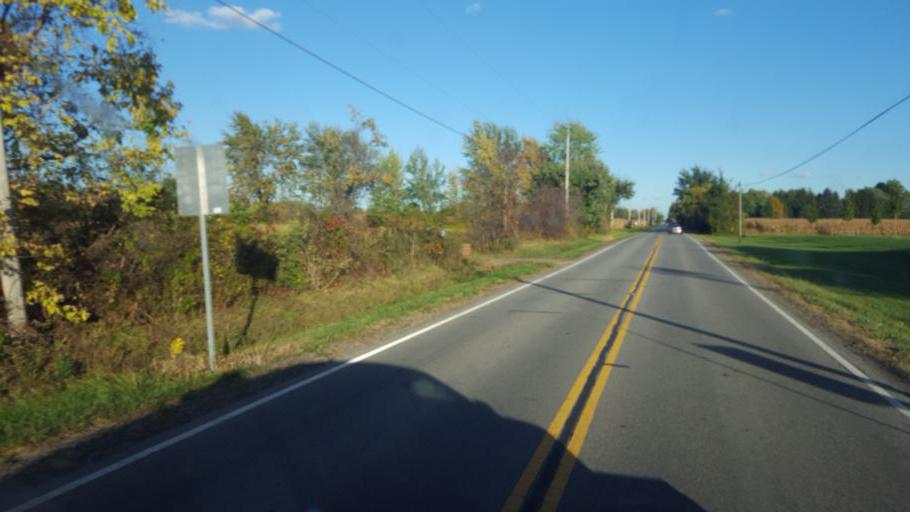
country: US
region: Ohio
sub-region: Franklin County
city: New Albany
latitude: 40.0175
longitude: -82.7646
